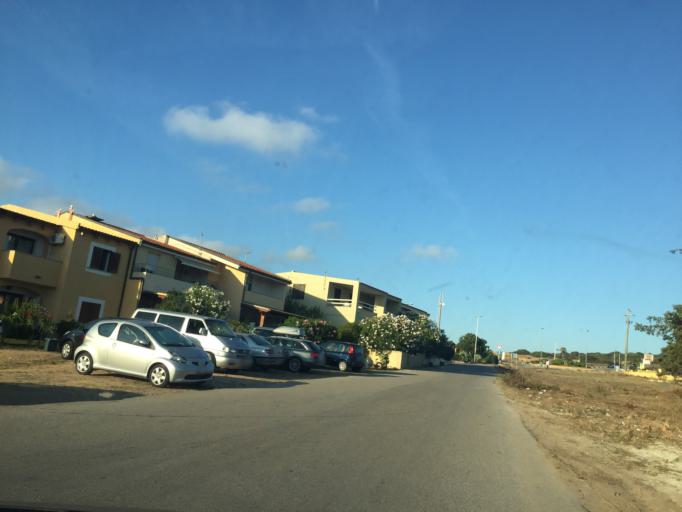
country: IT
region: Sardinia
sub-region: Provincia di Olbia-Tempio
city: Trinita d'Agultu
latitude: 41.0120
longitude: 8.8791
